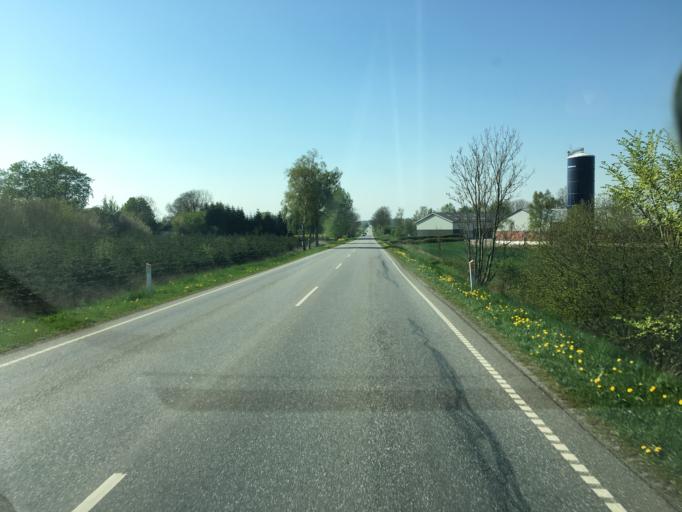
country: DK
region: South Denmark
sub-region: Haderslev Kommune
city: Vojens
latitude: 55.3071
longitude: 9.3503
